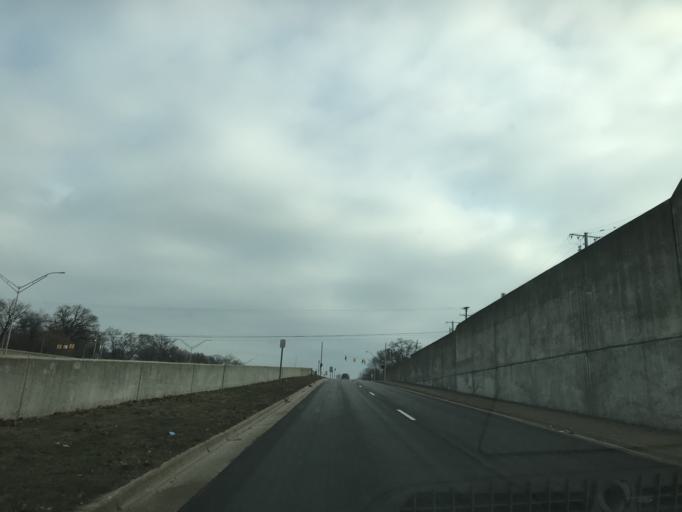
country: US
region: Michigan
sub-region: Oakland County
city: Pleasant Ridge
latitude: 42.4755
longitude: -83.1352
